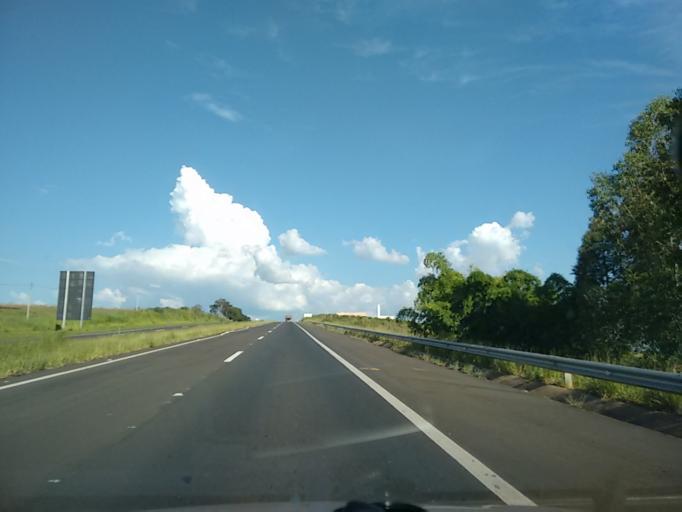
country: BR
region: Sao Paulo
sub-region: Garca
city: Garca
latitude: -22.2635
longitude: -49.5215
